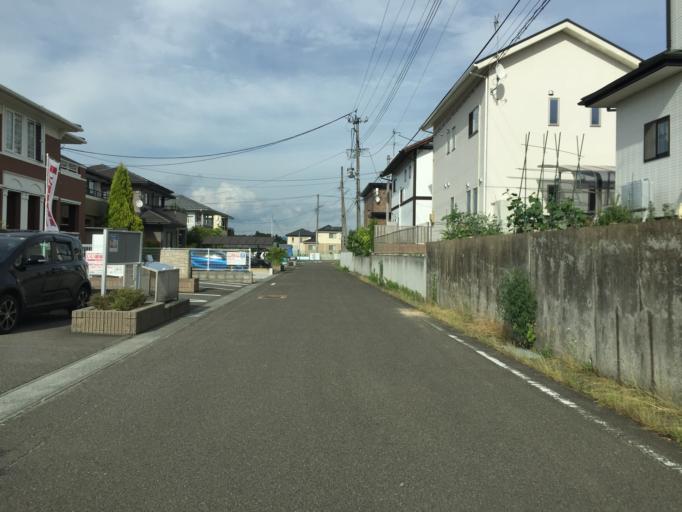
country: JP
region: Fukushima
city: Fukushima-shi
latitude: 37.6652
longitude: 140.4689
